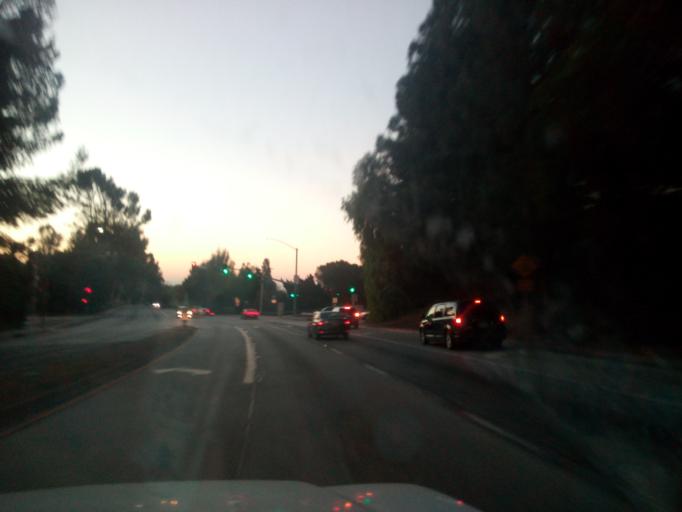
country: US
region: California
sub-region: Los Angeles County
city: Whittier
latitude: 33.9622
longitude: -118.0029
